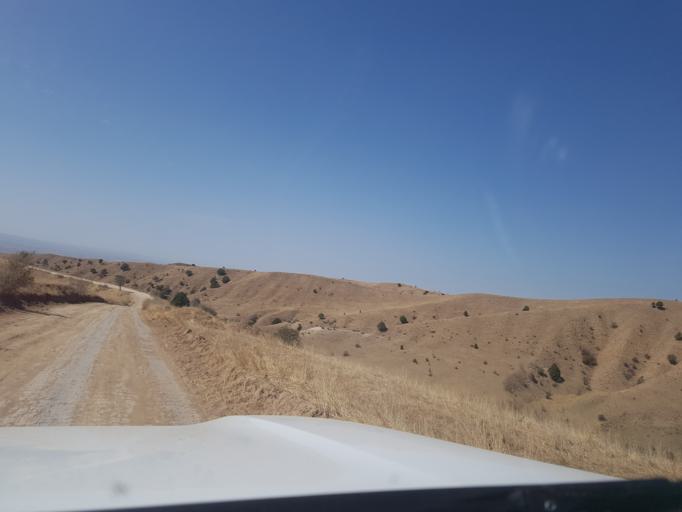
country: TM
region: Ahal
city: Baharly
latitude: 38.2973
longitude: 56.9379
